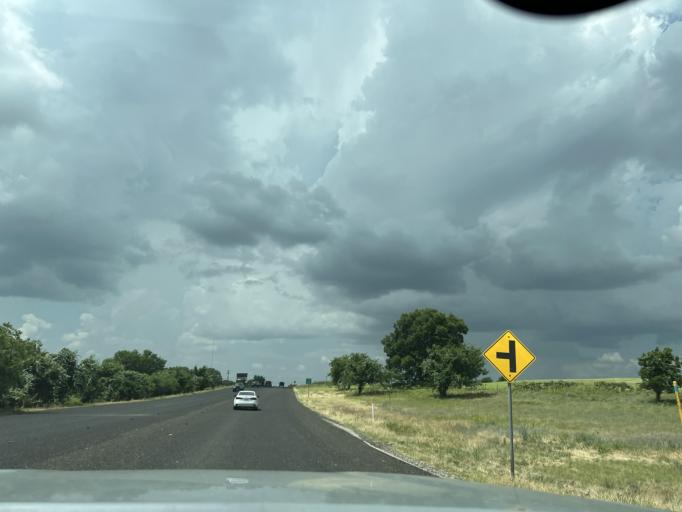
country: US
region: Texas
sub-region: Wise County
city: Decatur
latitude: 33.1981
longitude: -97.6059
